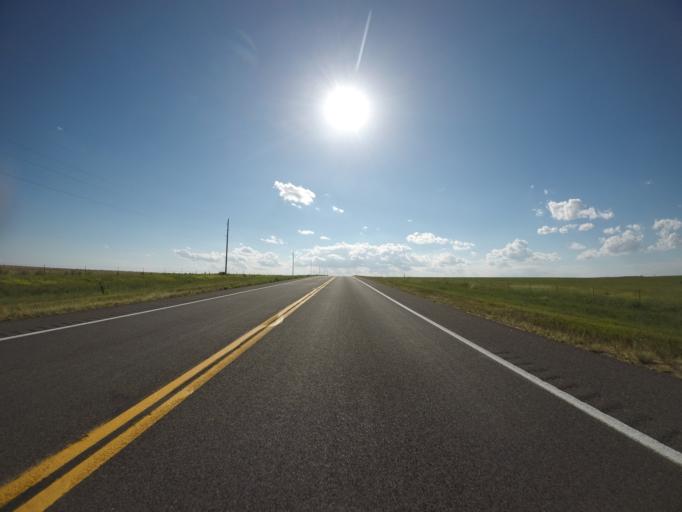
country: US
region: Colorado
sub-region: Morgan County
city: Fort Morgan
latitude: 40.6109
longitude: -103.7660
